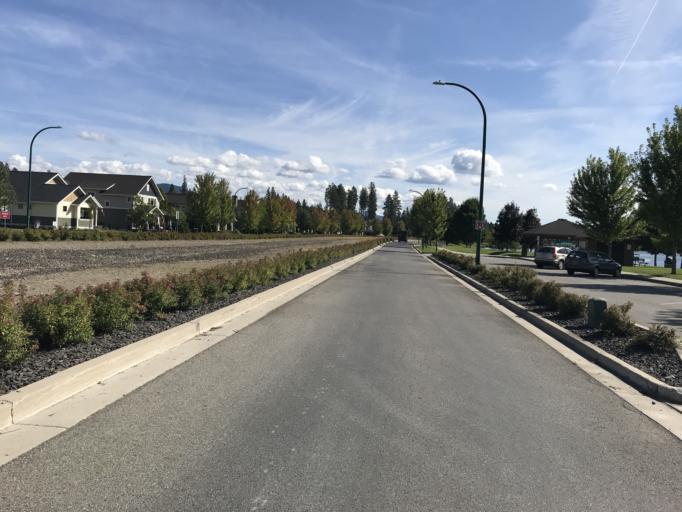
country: US
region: Idaho
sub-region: Kootenai County
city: Coeur d'Alene
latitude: 47.7009
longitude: -116.8447
